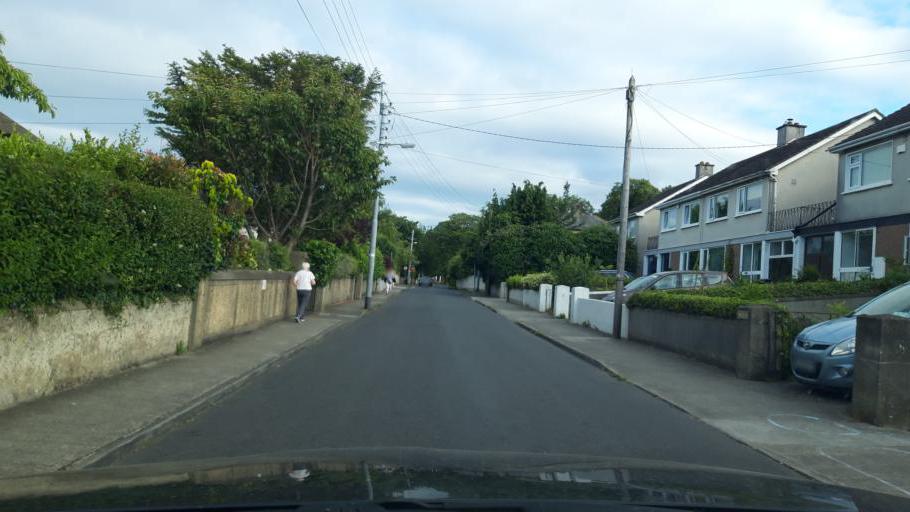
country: IE
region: Leinster
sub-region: Wicklow
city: Bray
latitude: 53.2021
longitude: -6.1023
